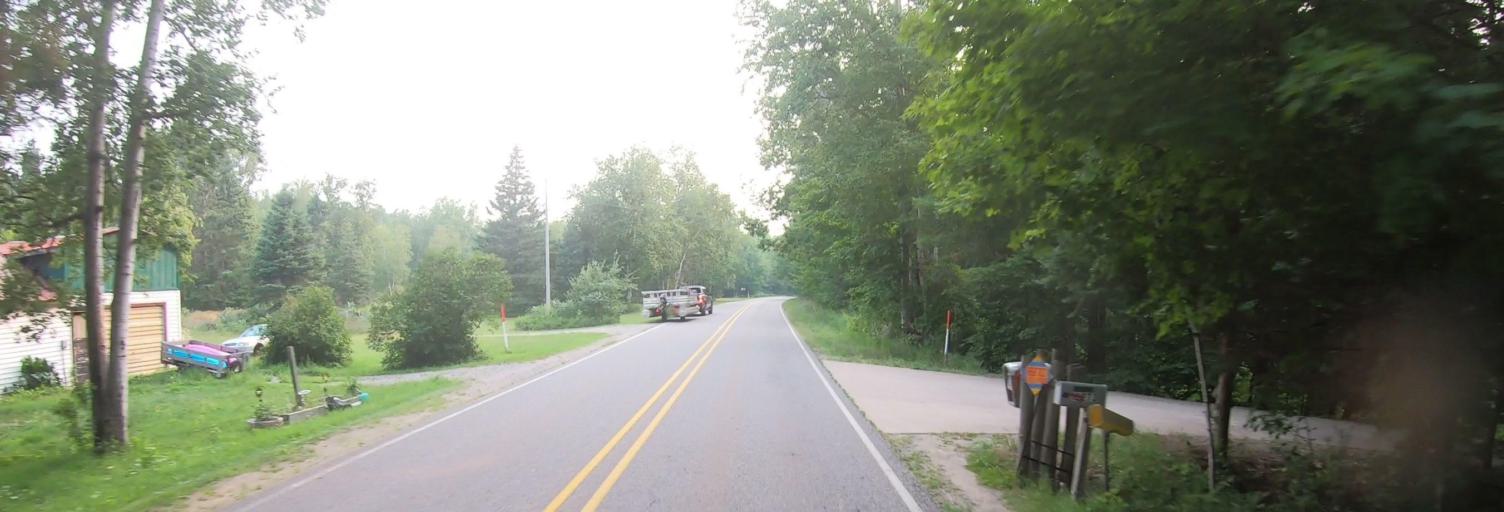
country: US
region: Michigan
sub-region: Chippewa County
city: Sault Ste. Marie
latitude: 46.4590
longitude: -84.7450
